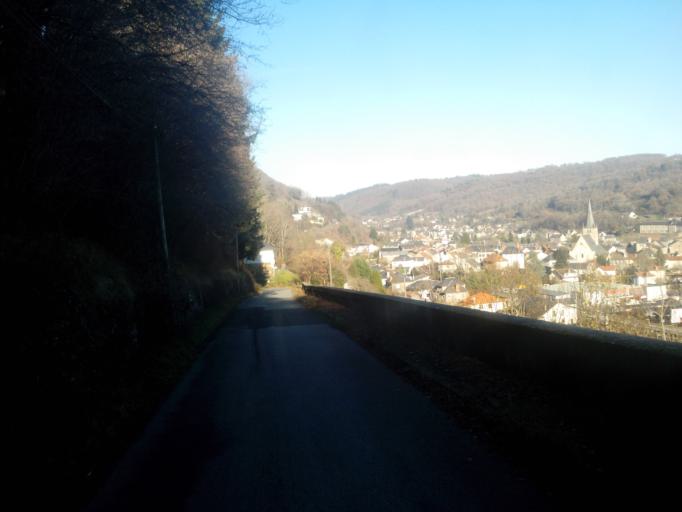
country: FR
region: Limousin
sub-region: Departement de la Correze
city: Bort-les-Orgues
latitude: 45.3977
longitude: 2.4903
